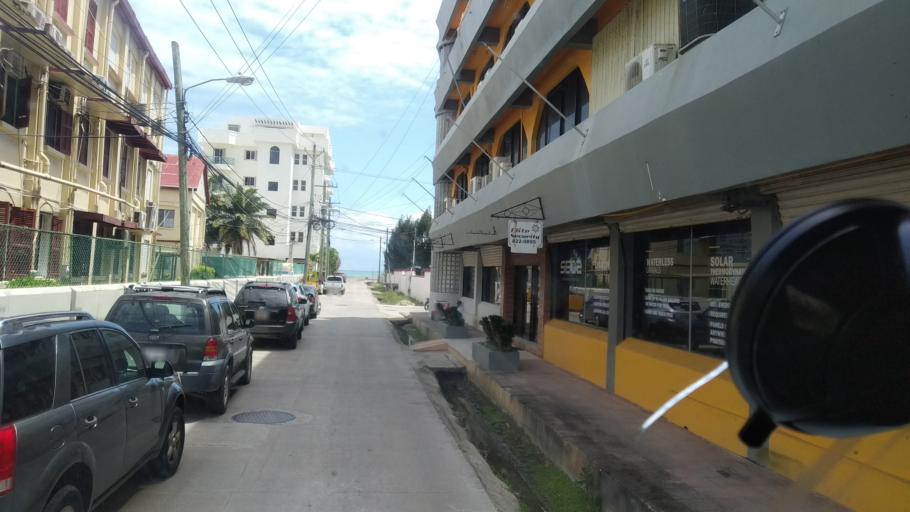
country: BZ
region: Belize
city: Belize City
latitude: 17.4965
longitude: -88.1829
